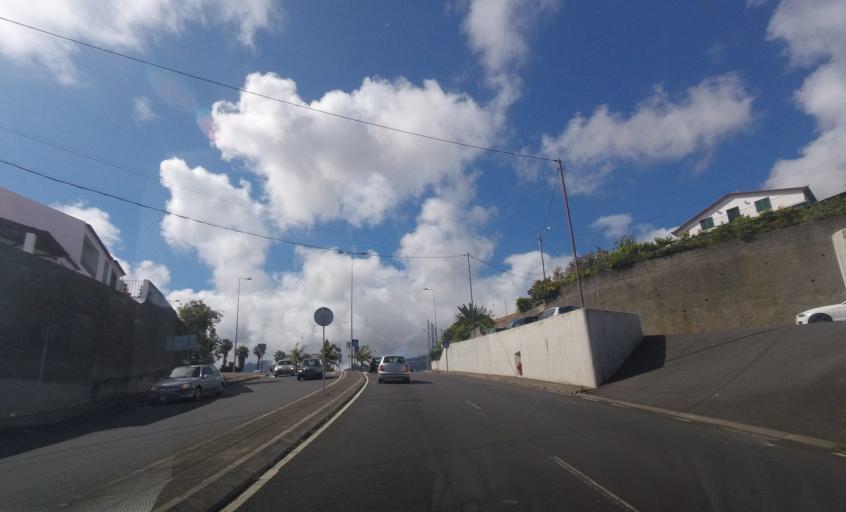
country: PT
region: Madeira
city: Camara de Lobos
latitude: 32.6504
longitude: -16.9407
